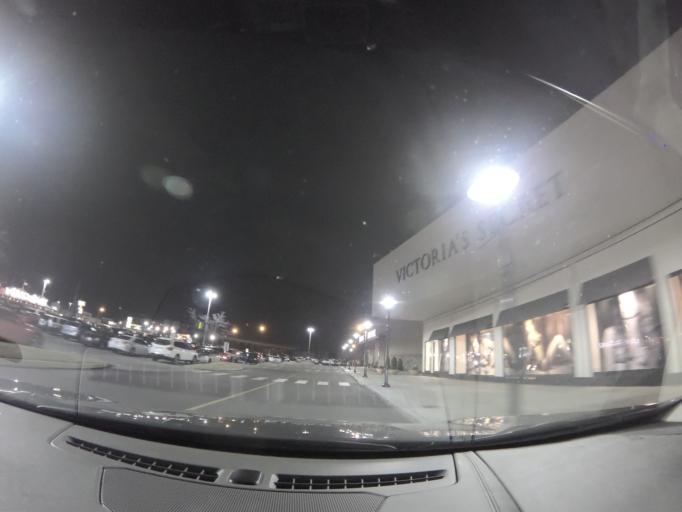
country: US
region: Kentucky
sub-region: Jefferson County
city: Beechwood Village
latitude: 38.2491
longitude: -85.6238
